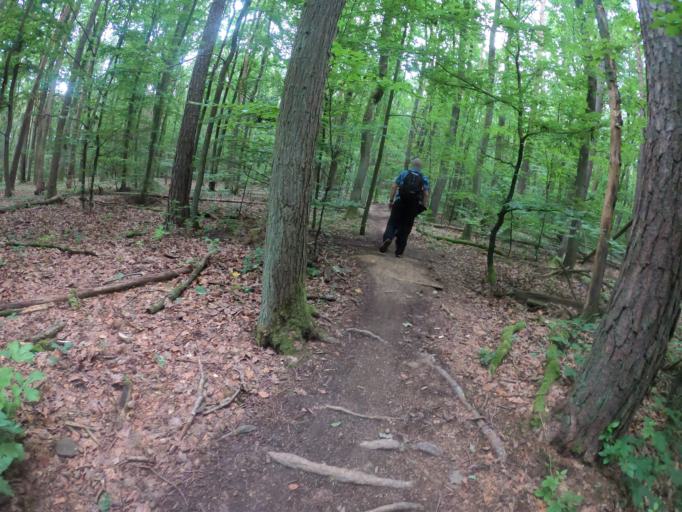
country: DE
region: Bavaria
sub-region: Upper Franconia
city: Litzendorf
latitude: 49.9257
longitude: 11.0121
